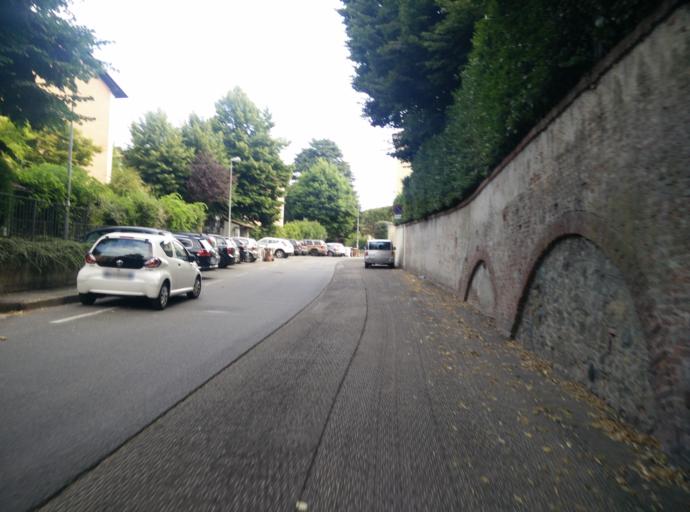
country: IT
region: Piedmont
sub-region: Provincia di Torino
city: Revigliasco
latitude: 44.9939
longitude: 7.7223
